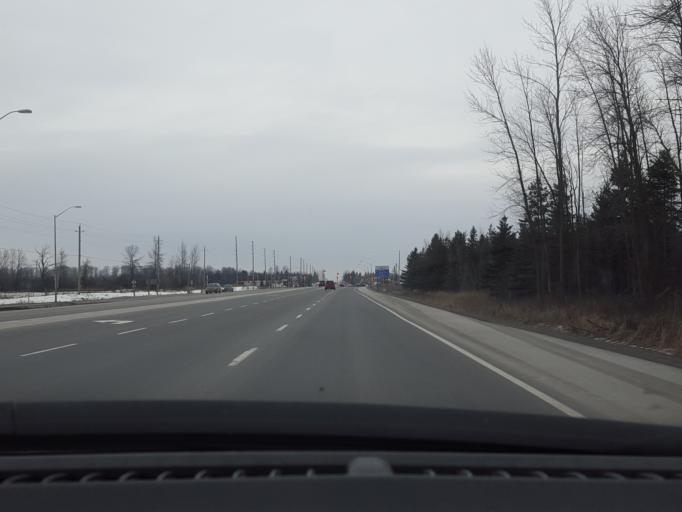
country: CA
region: Ontario
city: Keswick
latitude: 44.1945
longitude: -79.4386
